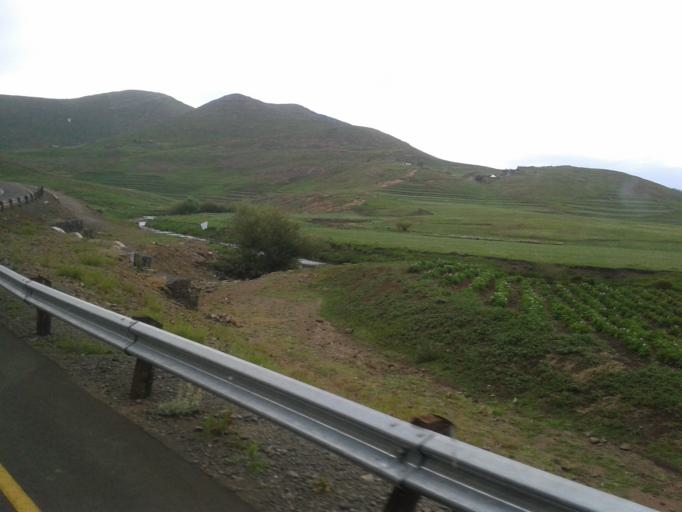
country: LS
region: Maseru
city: Nako
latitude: -29.8055
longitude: 28.0273
